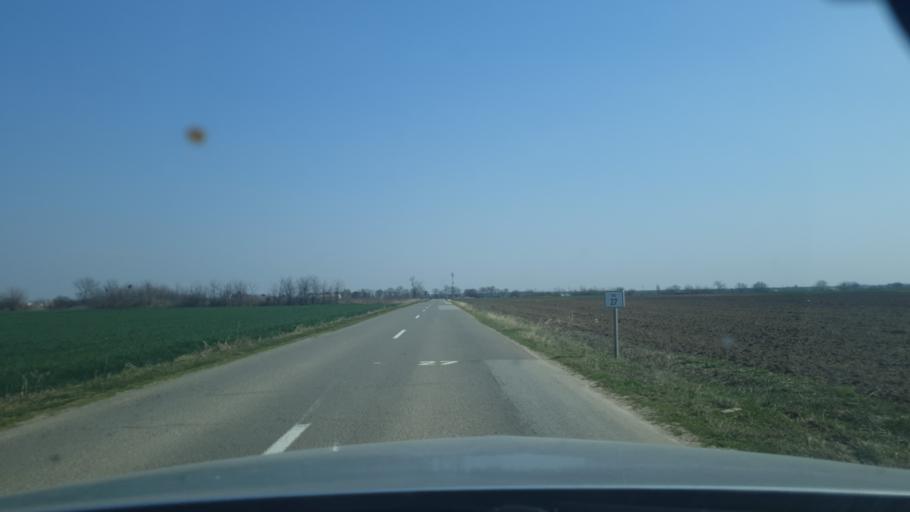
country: RS
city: Sasinci
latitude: 45.0477
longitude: 19.7122
